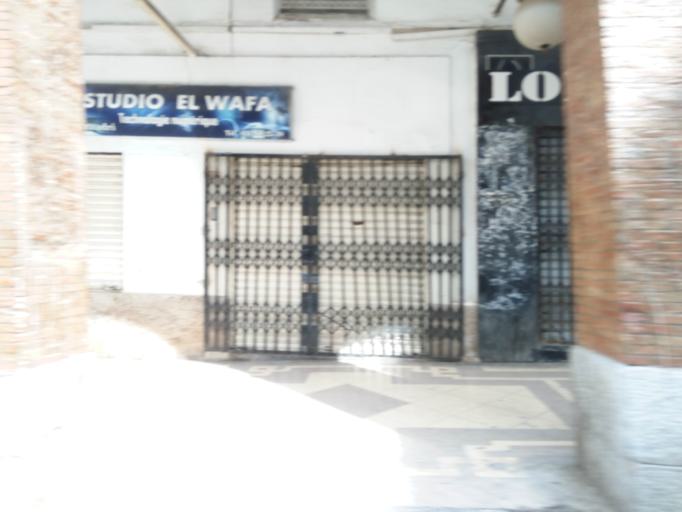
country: DZ
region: Constantine
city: Constantine
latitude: 36.3609
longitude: 6.6071
